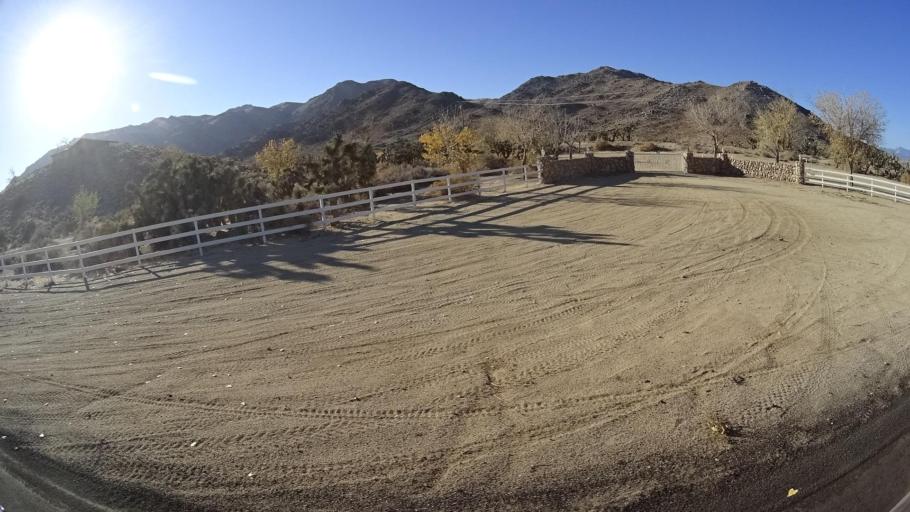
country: US
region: California
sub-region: Kern County
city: Weldon
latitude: 35.5082
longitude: -118.2038
